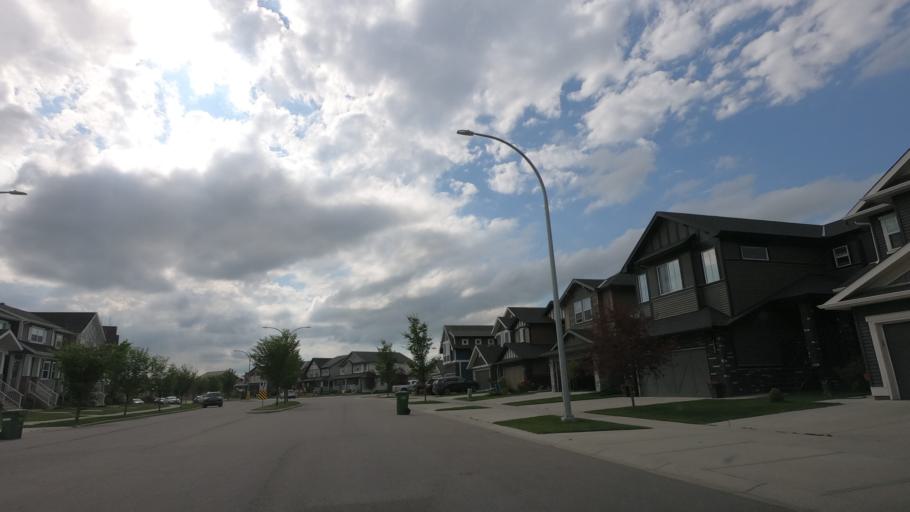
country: CA
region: Alberta
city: Airdrie
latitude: 51.2592
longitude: -113.9888
